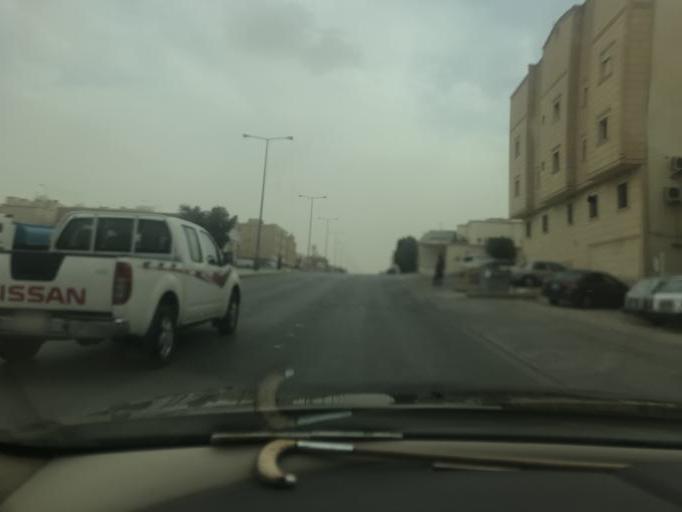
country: SA
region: Ar Riyad
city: Riyadh
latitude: 24.7866
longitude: 46.6939
